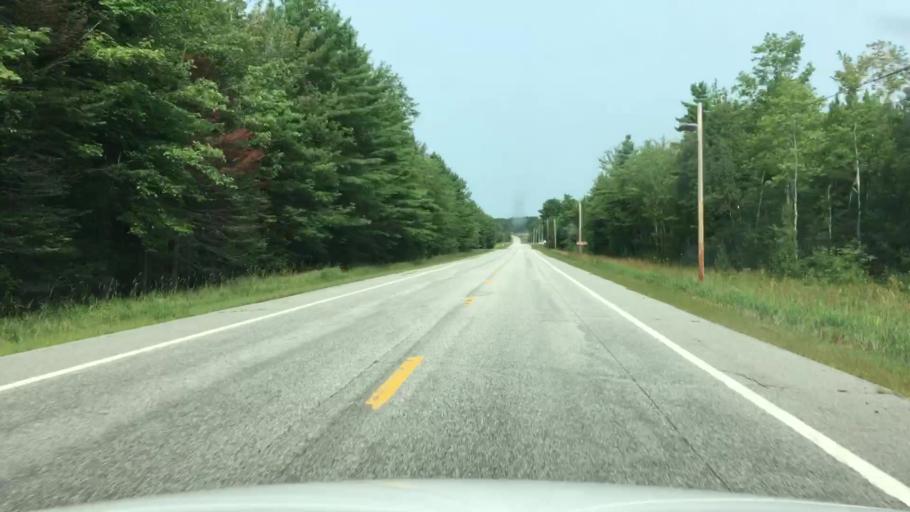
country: US
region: Maine
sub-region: Kennebec County
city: Wayne
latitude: 44.3856
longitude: -70.1078
